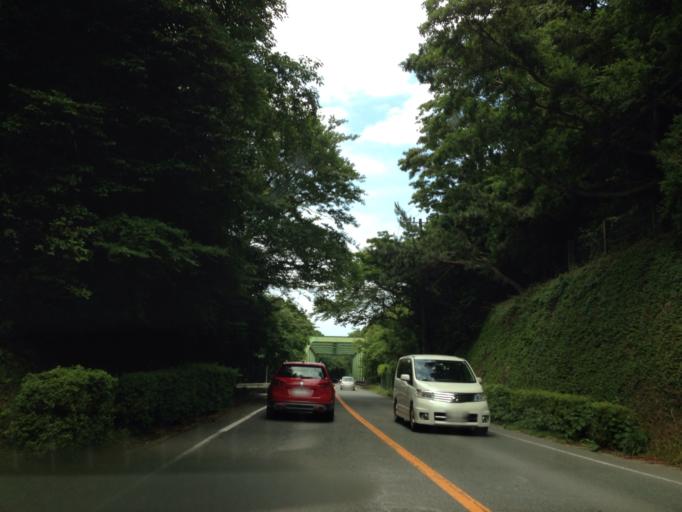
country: JP
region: Shizuoka
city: Heda
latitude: 34.9150
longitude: 138.8237
